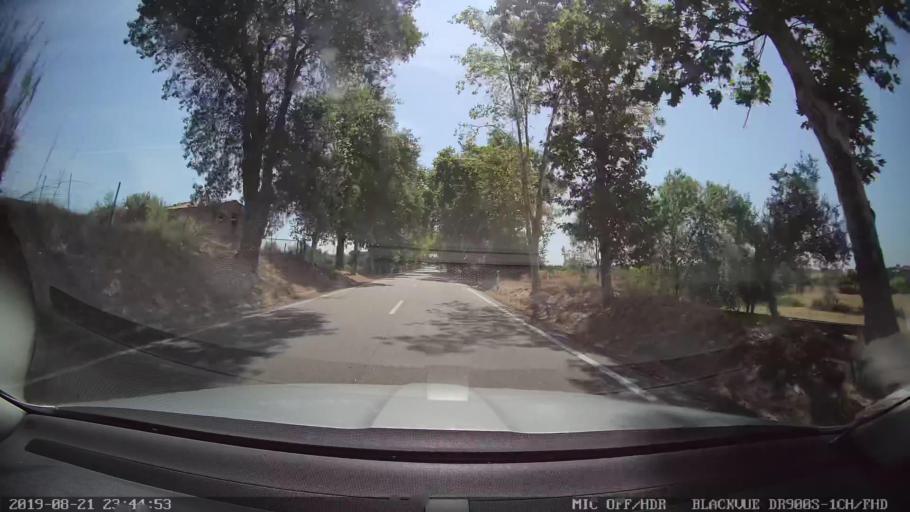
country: PT
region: Castelo Branco
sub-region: Idanha-A-Nova
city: Idanha-a-Nova
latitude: 39.8435
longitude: -7.2718
